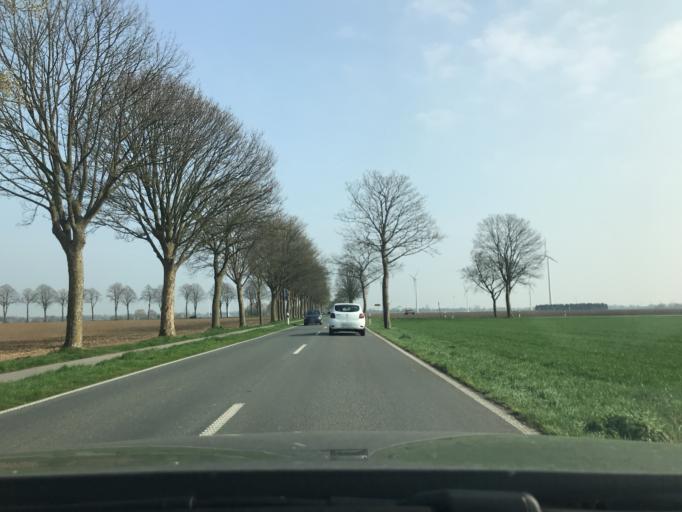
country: DE
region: North Rhine-Westphalia
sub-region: Regierungsbezirk Dusseldorf
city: Goch
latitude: 51.7222
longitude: 6.2170
